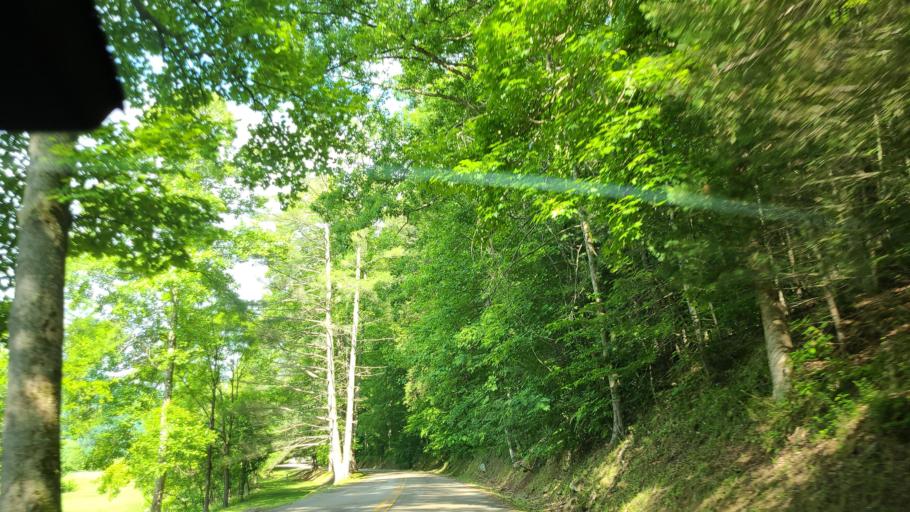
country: US
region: Kentucky
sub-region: Bell County
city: Pineville
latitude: 36.7433
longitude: -83.6977
